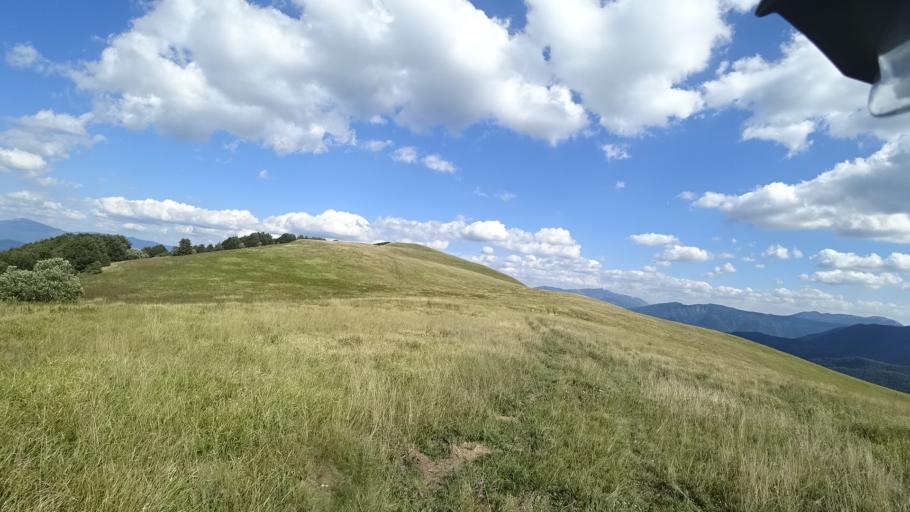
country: HR
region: Zadarska
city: Gracac
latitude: 44.3741
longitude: 16.0528
